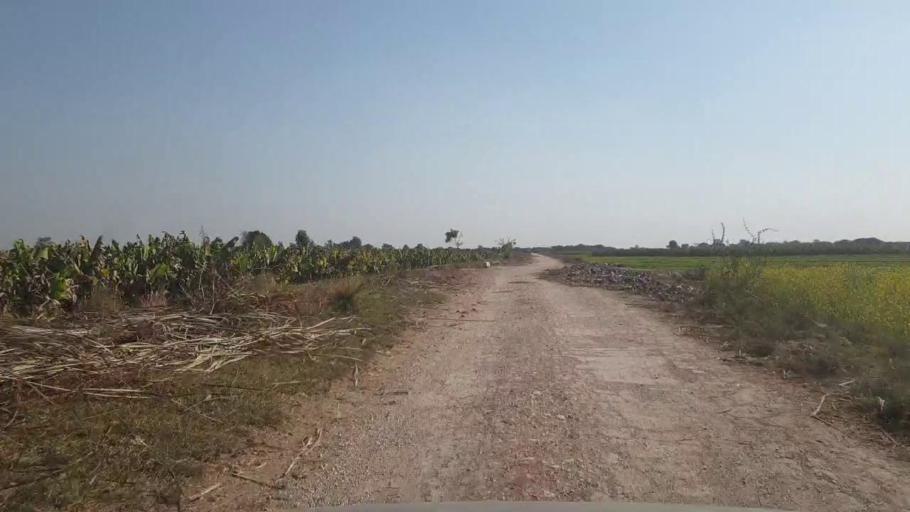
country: PK
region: Sindh
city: Chambar
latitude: 25.3163
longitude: 68.8722
